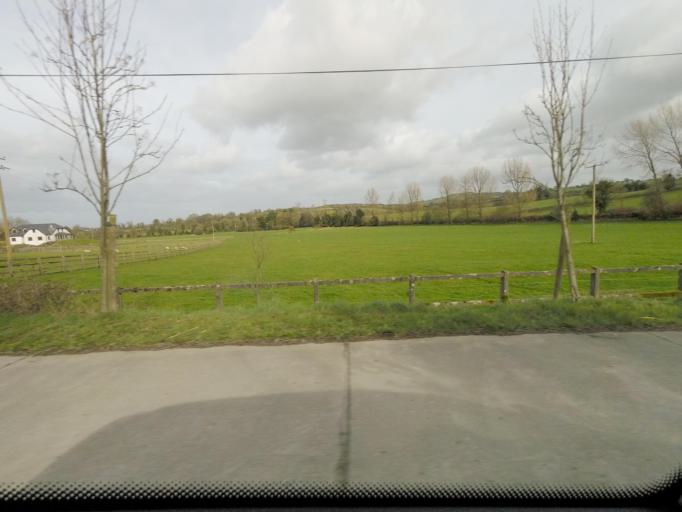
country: IE
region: Leinster
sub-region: Kildare
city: Eadestown
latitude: 53.1996
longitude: -6.5730
